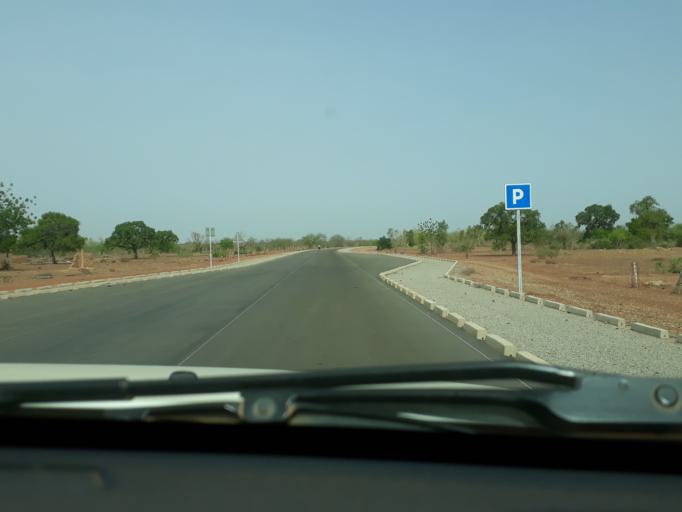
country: BF
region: Plateau-Central
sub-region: Province d'Oubritenga
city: Ziniare
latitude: 12.5499
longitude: -1.3973
